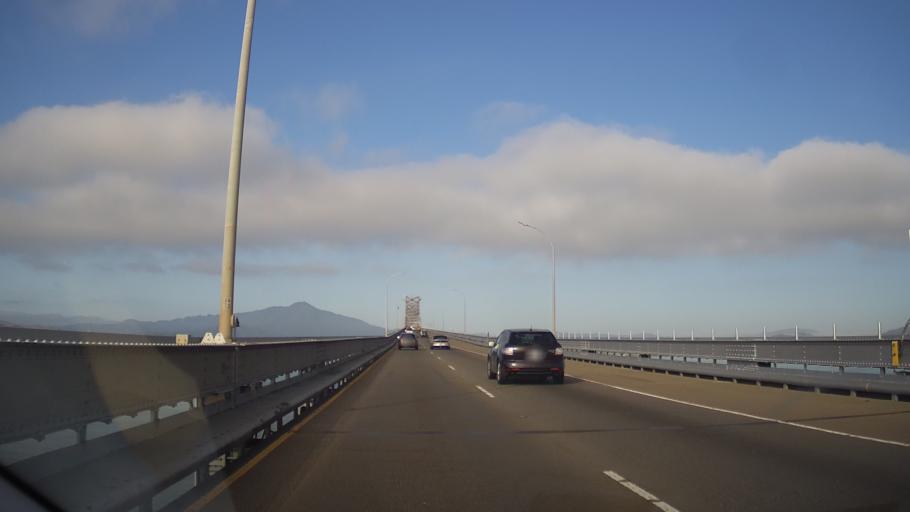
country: US
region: California
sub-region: Marin County
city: Tiburon
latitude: 37.9341
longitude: -122.4342
